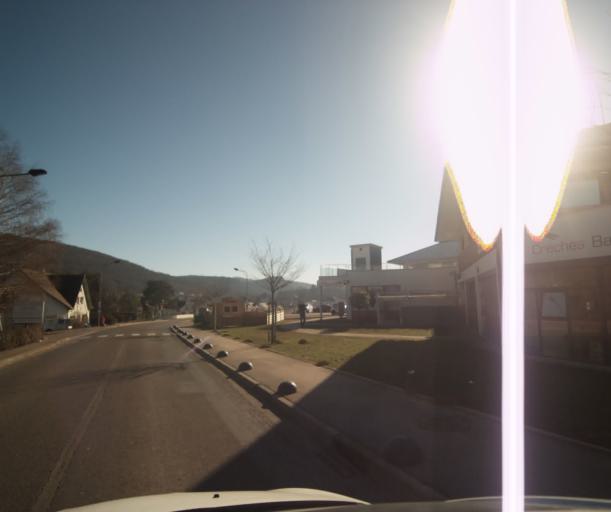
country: FR
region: Franche-Comte
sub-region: Departement du Doubs
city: Avanne-Aveney
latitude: 47.2134
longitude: 5.9625
